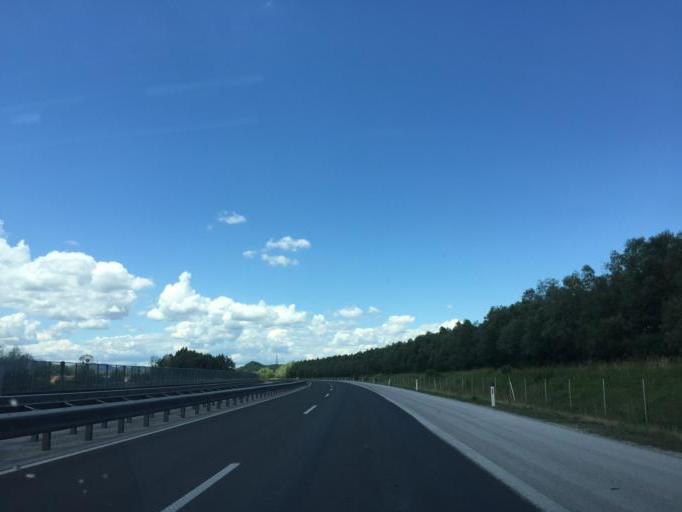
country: SI
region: Sveti Jurij v Slovenskih Goricah
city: Jurovski Dol
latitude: 46.5804
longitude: 15.7322
